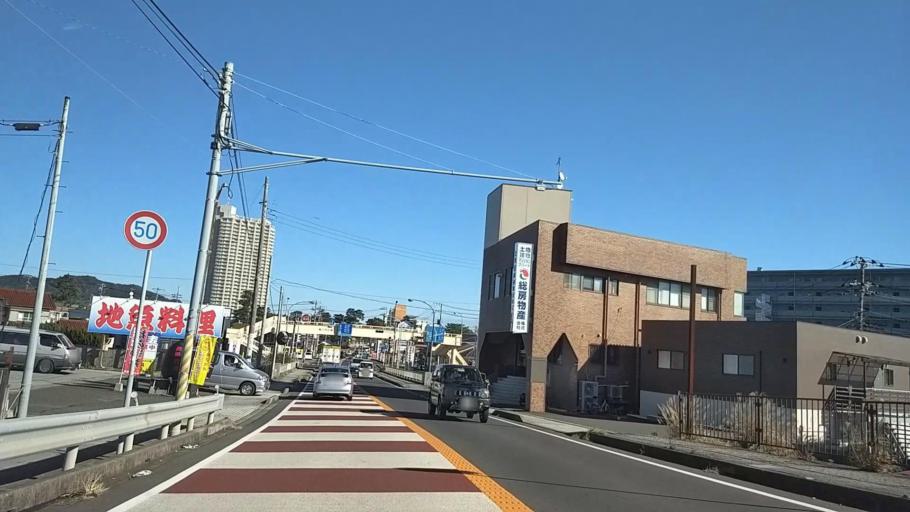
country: JP
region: Chiba
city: Kawaguchi
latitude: 35.1098
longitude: 140.1067
